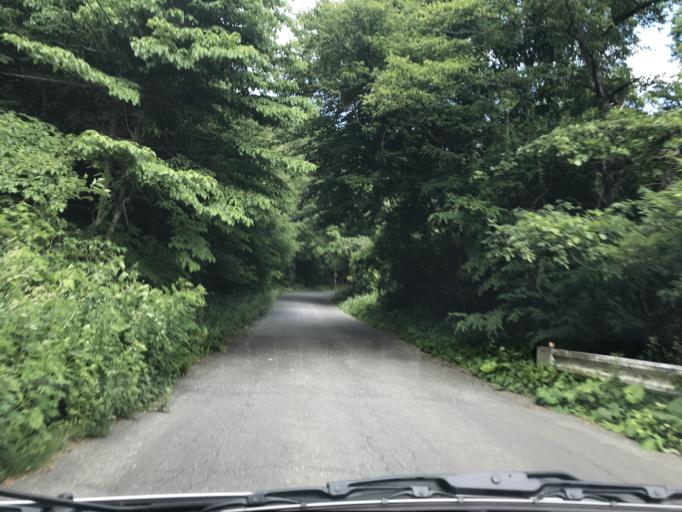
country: JP
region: Iwate
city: Ichinoseki
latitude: 38.8821
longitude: 140.9075
